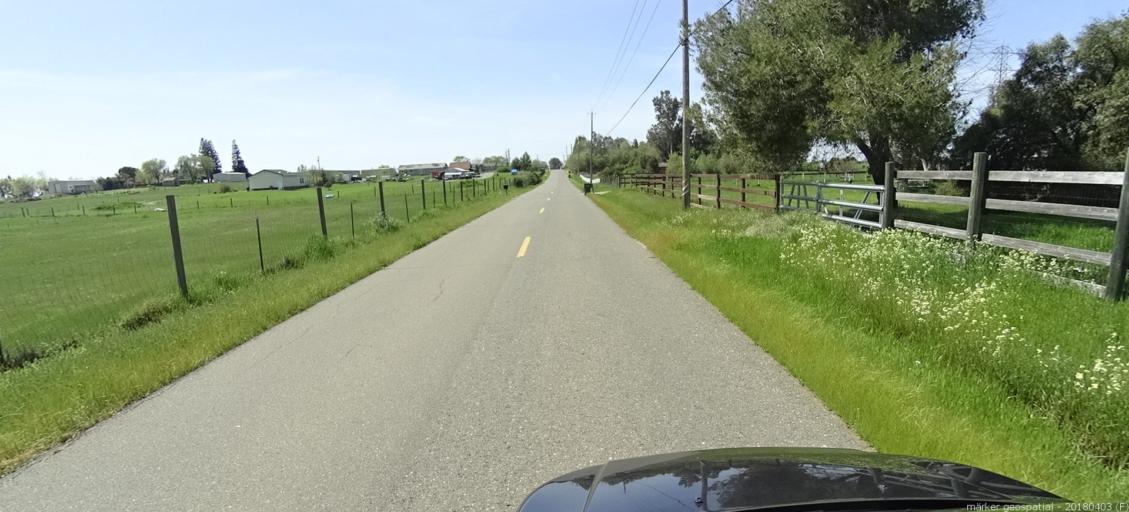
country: US
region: California
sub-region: Sacramento County
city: Herald
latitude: 38.3505
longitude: -121.2250
